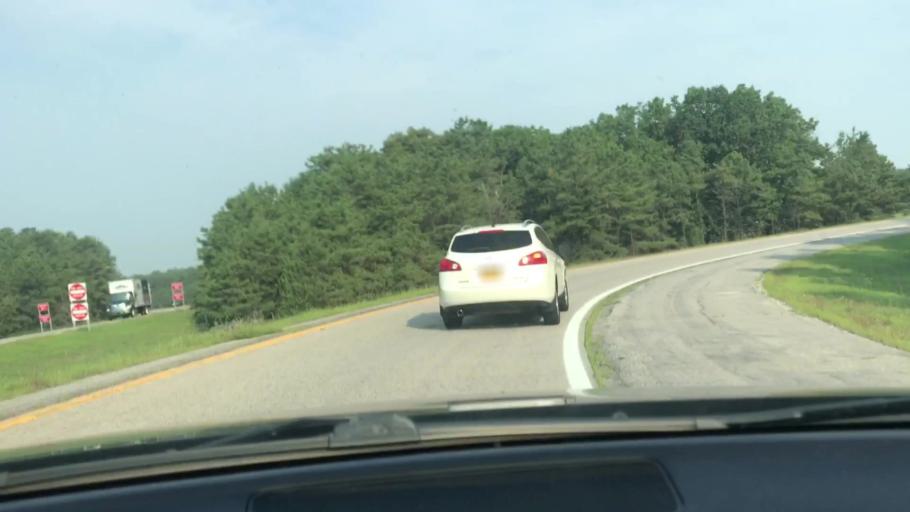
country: US
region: New York
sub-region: Suffolk County
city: Flanders
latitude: 40.8688
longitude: -72.6186
